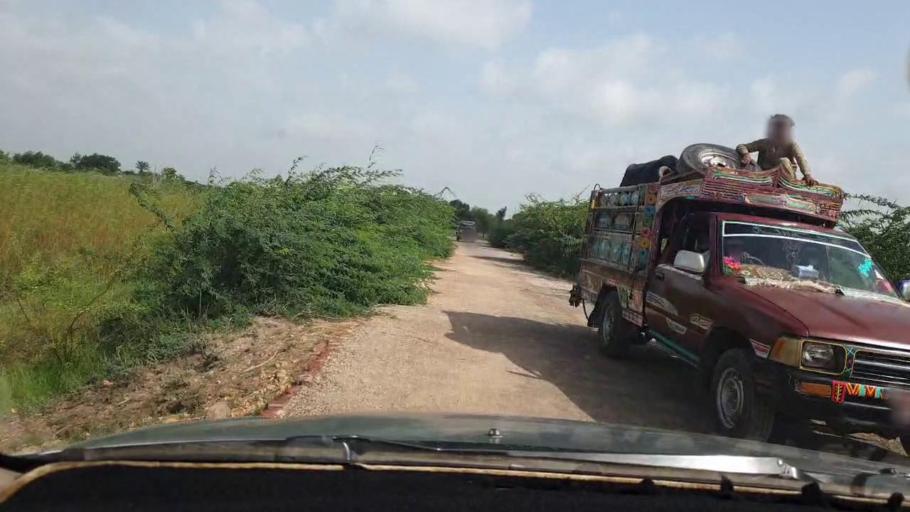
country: PK
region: Sindh
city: Tando Bago
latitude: 24.7798
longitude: 68.9825
